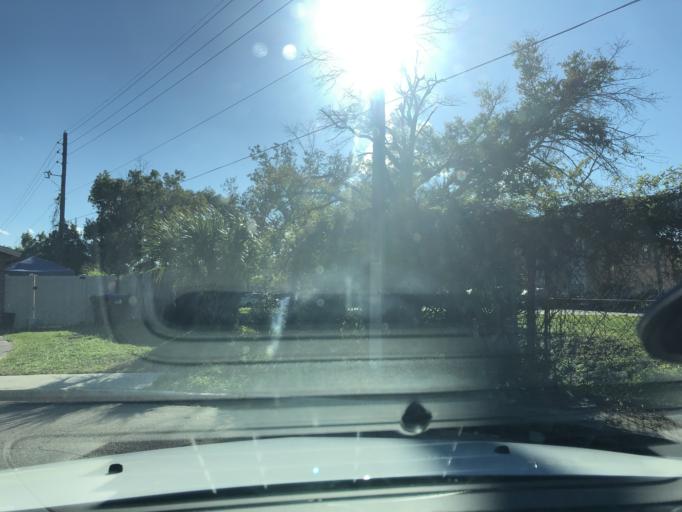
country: US
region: Florida
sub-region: Orange County
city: Oak Ridge
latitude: 28.4785
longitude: -81.4296
